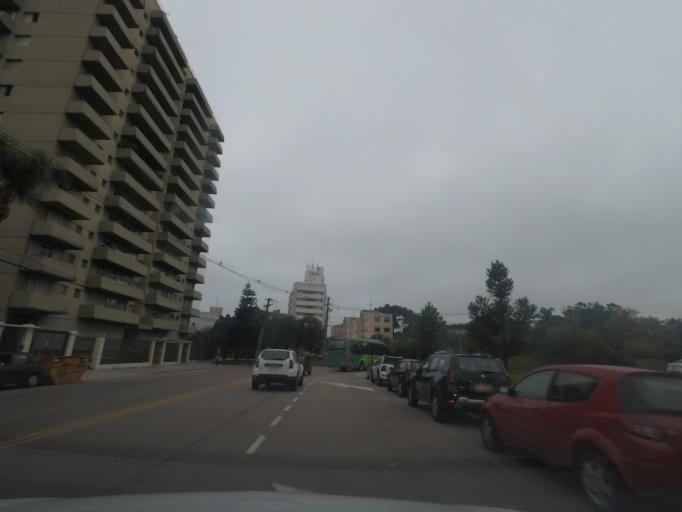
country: BR
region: Parana
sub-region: Curitiba
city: Curitiba
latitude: -25.4162
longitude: -49.2697
